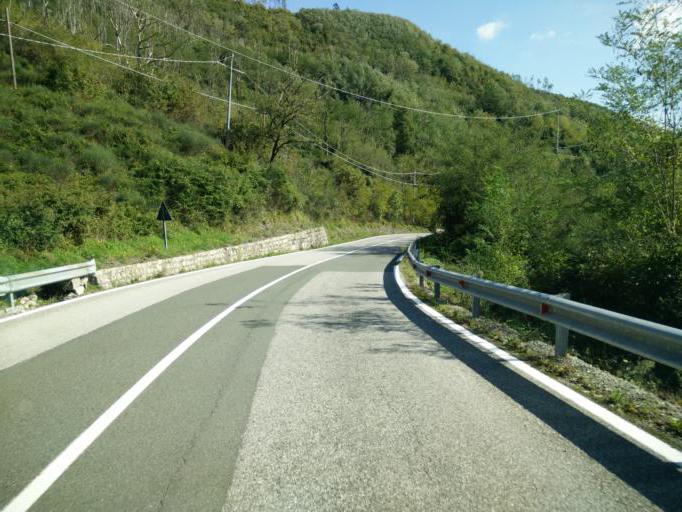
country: IT
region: Liguria
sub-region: Provincia di La Spezia
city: Carrodano
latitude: 44.2480
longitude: 9.6432
